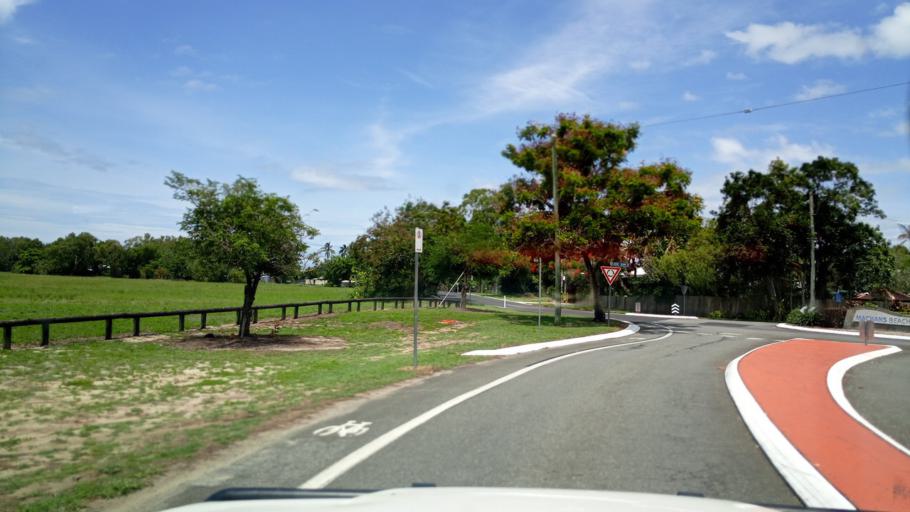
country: AU
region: Queensland
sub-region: Cairns
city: Redlynch
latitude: -16.8522
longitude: 145.7455
